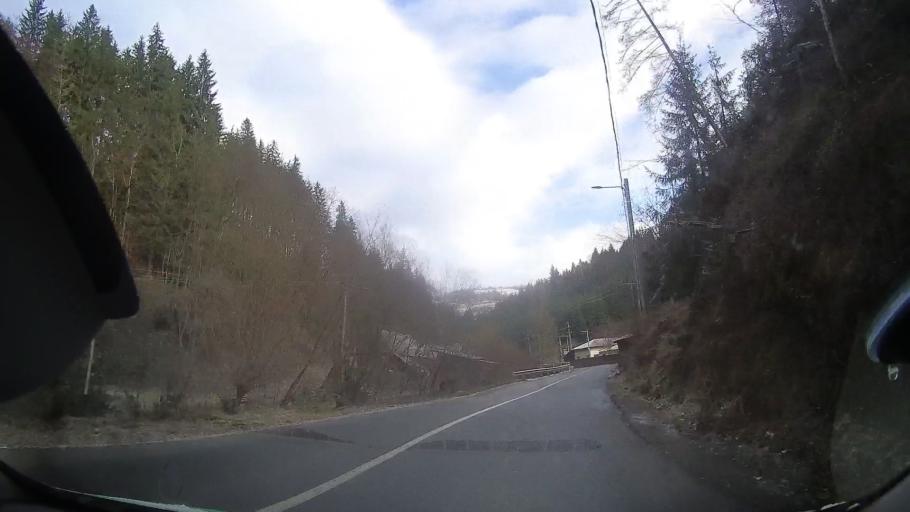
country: RO
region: Alba
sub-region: Comuna Albac
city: Albac
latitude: 46.4666
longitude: 22.9670
